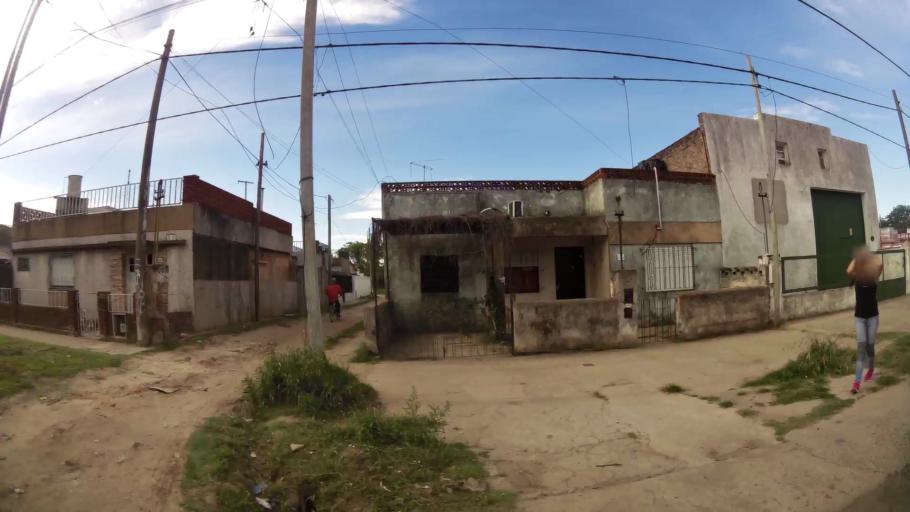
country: AR
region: Santa Fe
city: Granadero Baigorria
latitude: -32.9161
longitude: -60.7144
